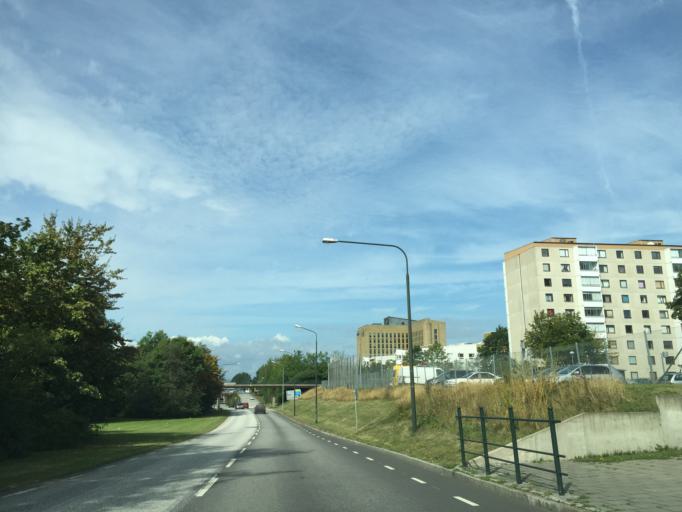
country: SE
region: Skane
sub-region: Burlovs Kommun
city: Arloev
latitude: 55.5839
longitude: 13.0525
